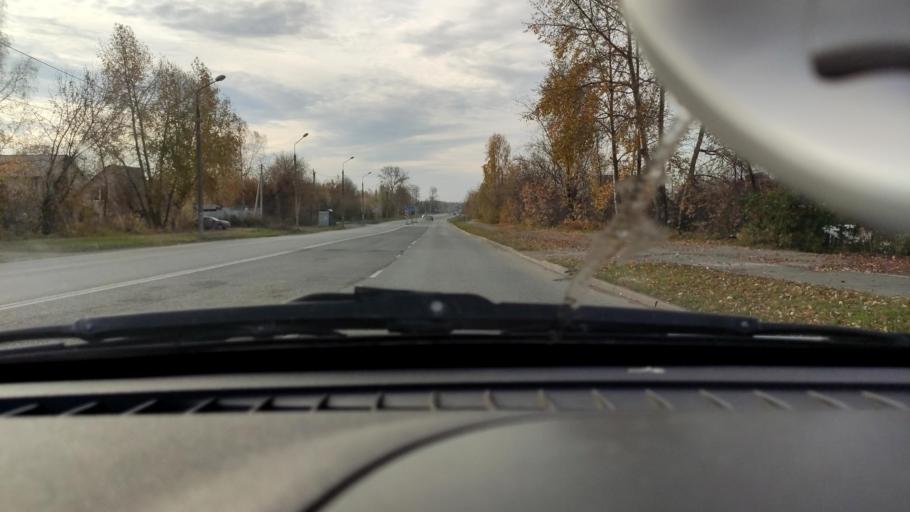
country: RU
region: Perm
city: Polazna
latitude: 58.1217
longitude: 56.4035
